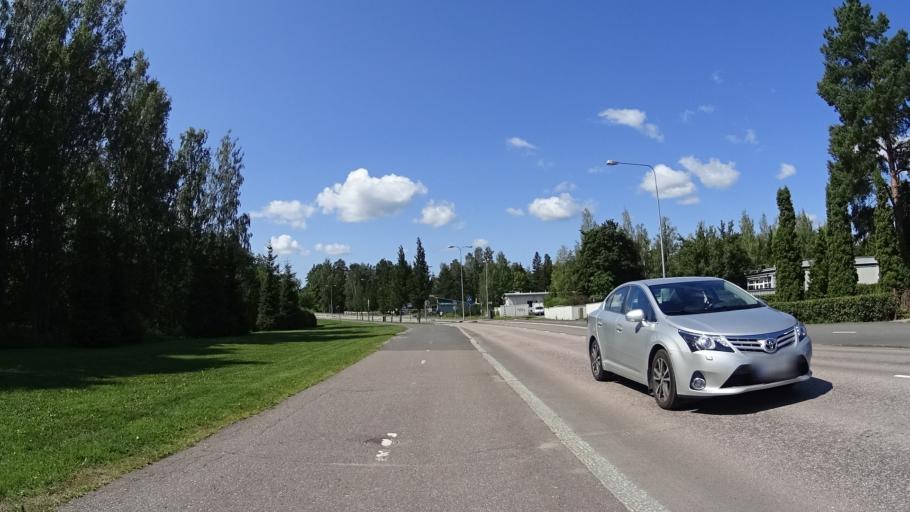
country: FI
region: Uusimaa
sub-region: Helsinki
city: Jaervenpaeae
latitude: 60.4710
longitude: 25.0777
